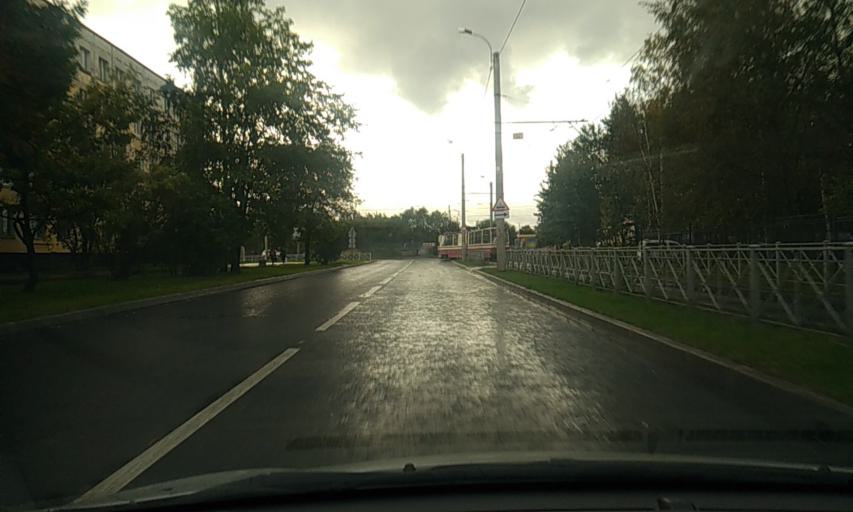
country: RU
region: St.-Petersburg
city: Sosnovaya Polyana
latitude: 59.8266
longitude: 30.1402
